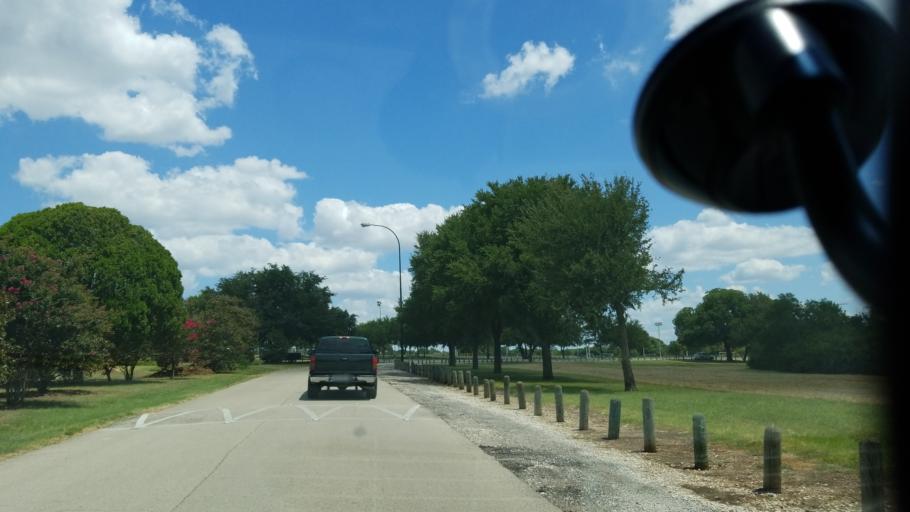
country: US
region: Texas
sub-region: Dallas County
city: Cockrell Hill
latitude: 32.7072
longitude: -96.8542
